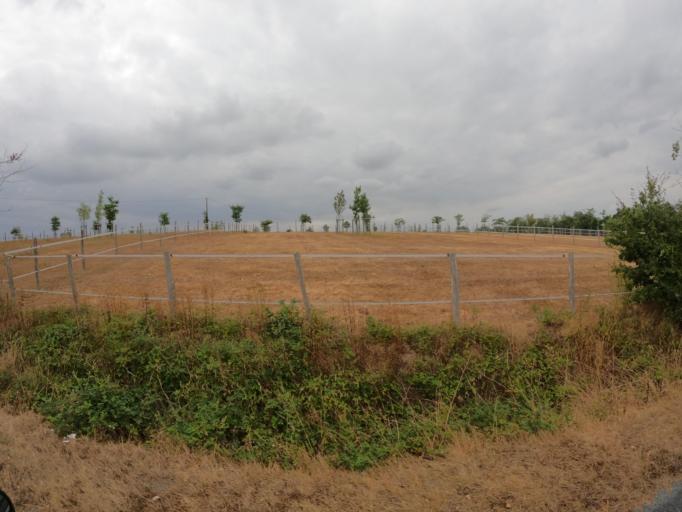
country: FR
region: Pays de la Loire
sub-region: Departement de la Vendee
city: Tiffauges
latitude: 46.9904
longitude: -1.1096
